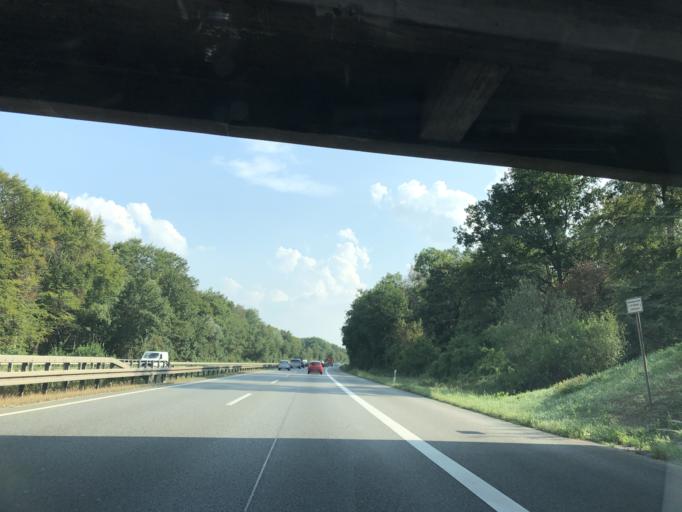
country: DE
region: Hesse
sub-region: Regierungsbezirk Darmstadt
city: Nauheim
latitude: 49.9554
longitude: 8.4757
